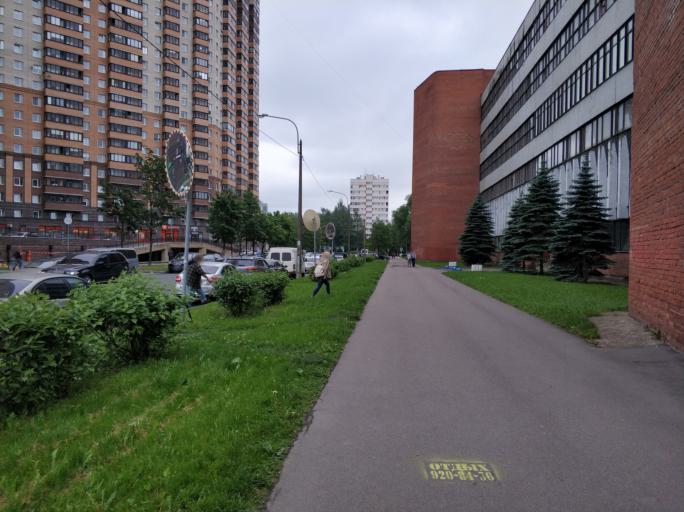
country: RU
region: St.-Petersburg
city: Grazhdanka
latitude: 60.0321
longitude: 30.4029
